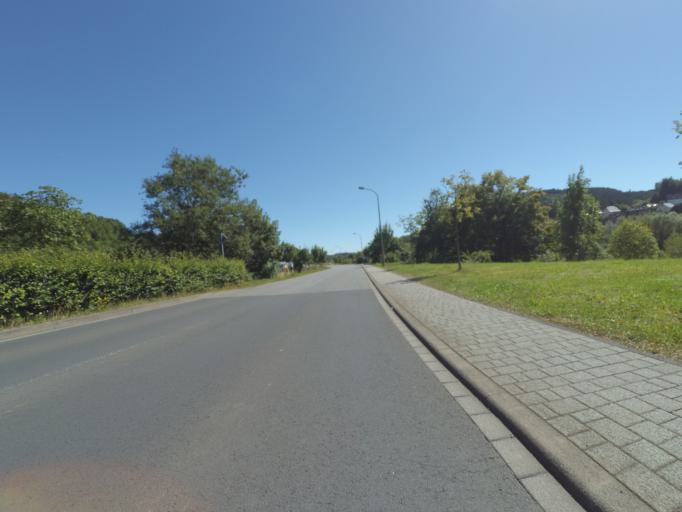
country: DE
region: Rheinland-Pfalz
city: Junkerath
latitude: 50.3487
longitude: 6.5739
